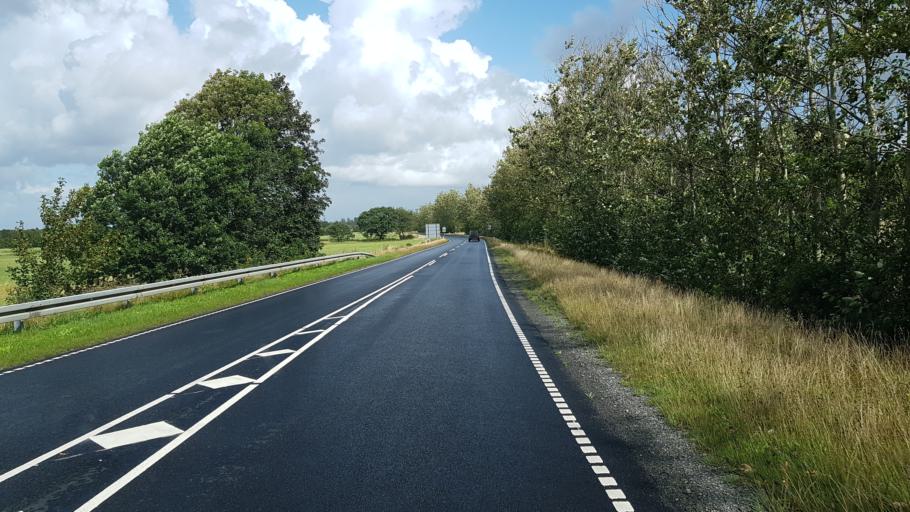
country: DK
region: South Denmark
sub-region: Vejen Kommune
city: Vejen
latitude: 55.4955
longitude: 9.1311
